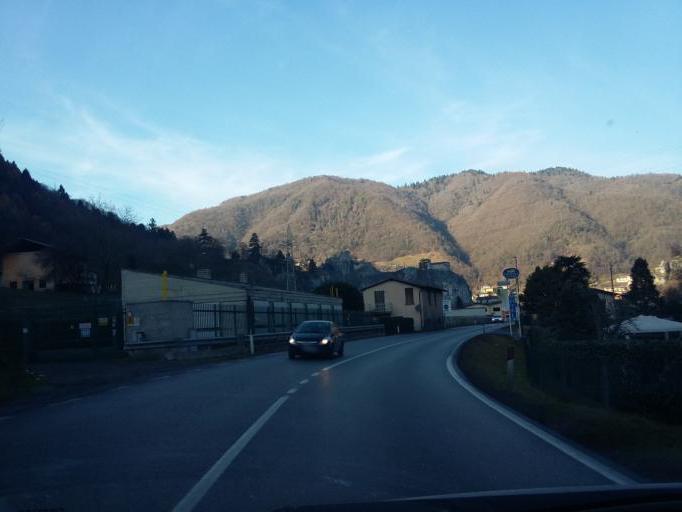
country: IT
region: Lombardy
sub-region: Provincia di Brescia
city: Vestone
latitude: 45.6968
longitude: 10.3889
